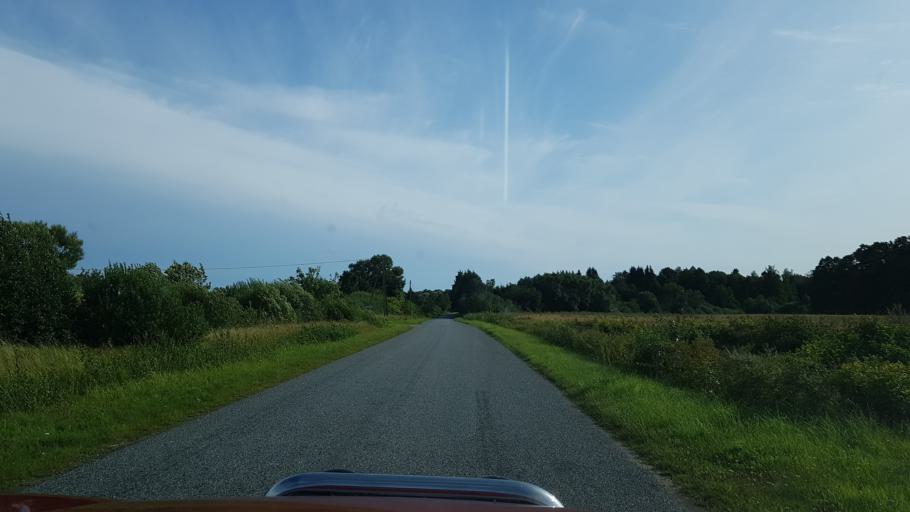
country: EE
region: Laeaene
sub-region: Lihula vald
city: Lihula
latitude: 58.4292
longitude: 24.0066
